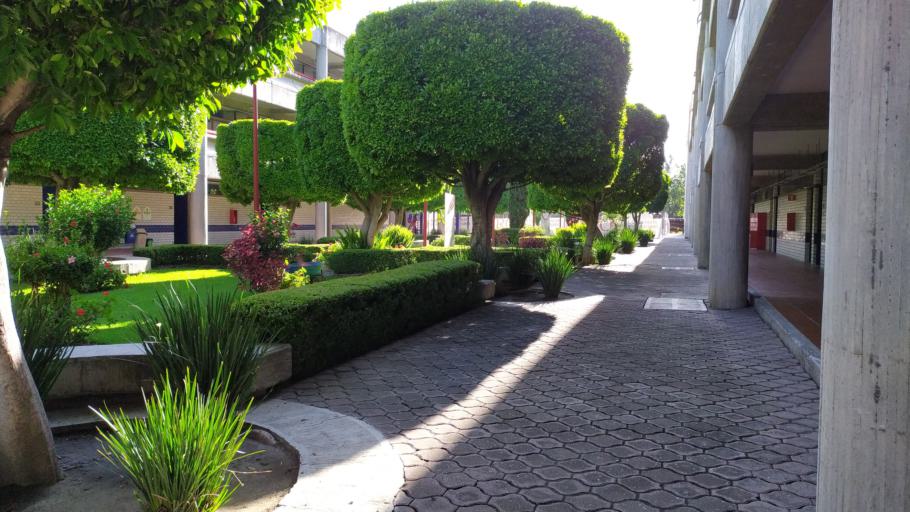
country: MX
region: Puebla
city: Puebla
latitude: 19.0310
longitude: -98.2410
